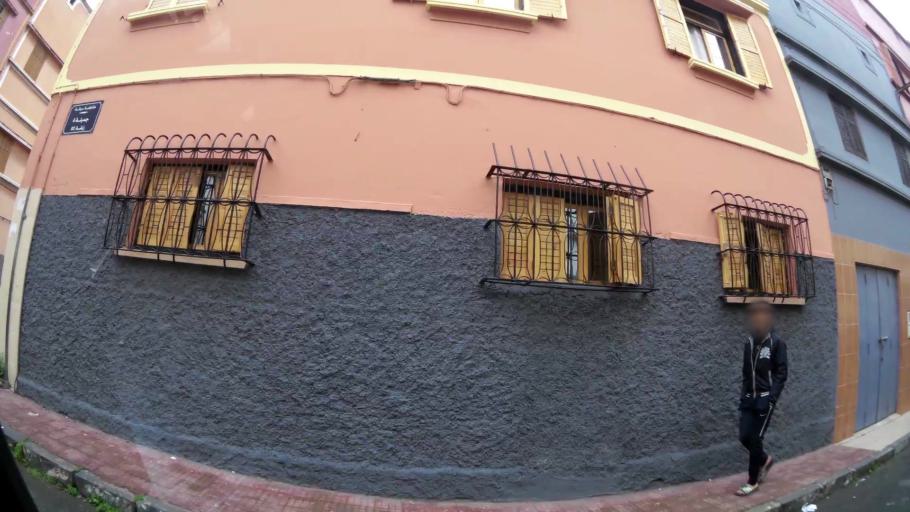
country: MA
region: Grand Casablanca
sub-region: Casablanca
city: Casablanca
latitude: 33.5469
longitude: -7.5696
